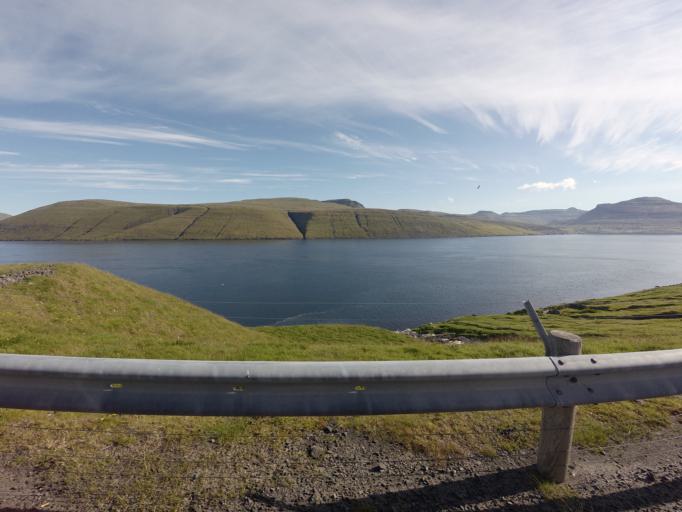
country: FO
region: Streymoy
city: Vestmanna
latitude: 62.1006
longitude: -7.1358
